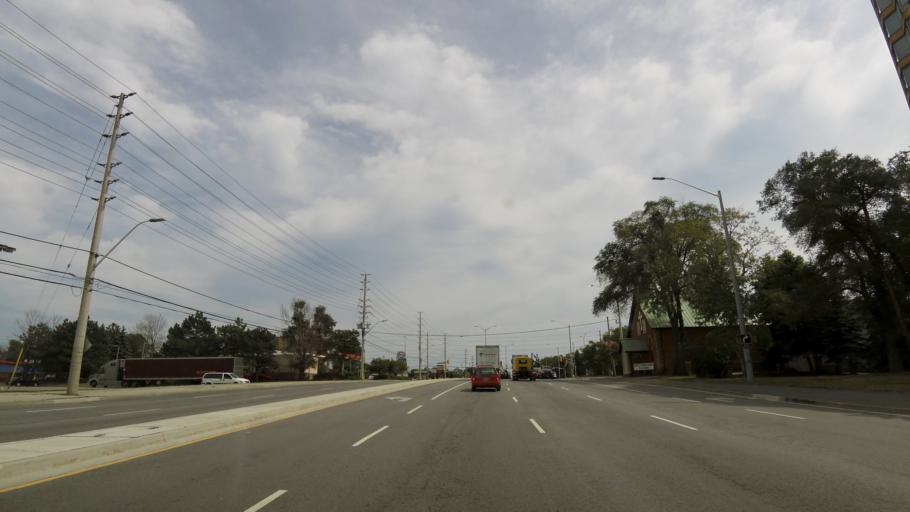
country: CA
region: Ontario
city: Etobicoke
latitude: 43.6236
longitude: -79.6039
